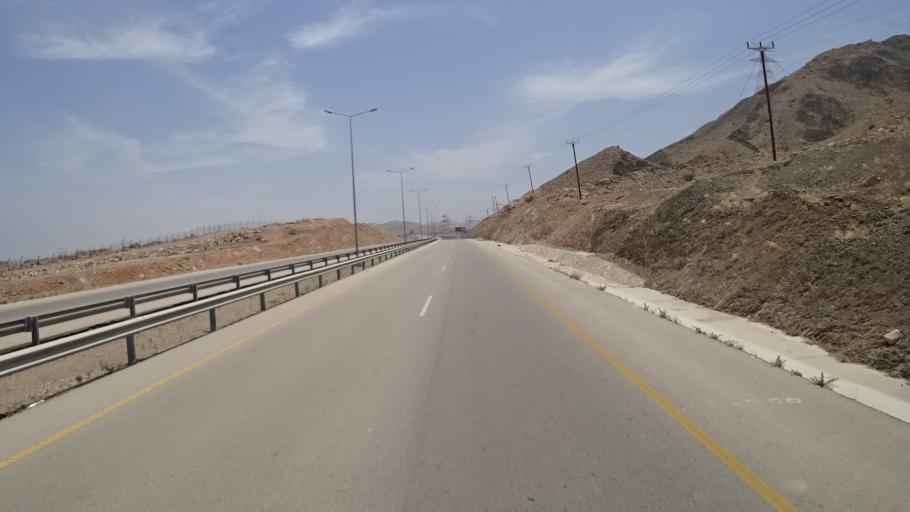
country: OM
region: Ash Sharqiyah
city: Sur
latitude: 22.6604
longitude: 59.3908
